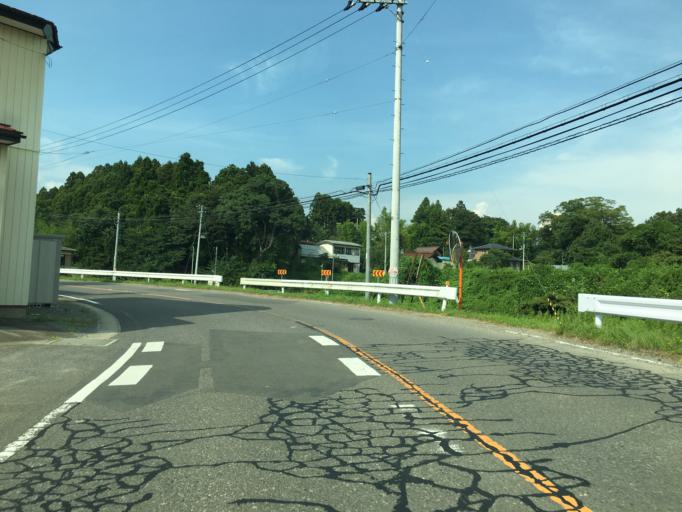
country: JP
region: Fukushima
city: Koriyama
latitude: 37.3511
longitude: 140.4155
